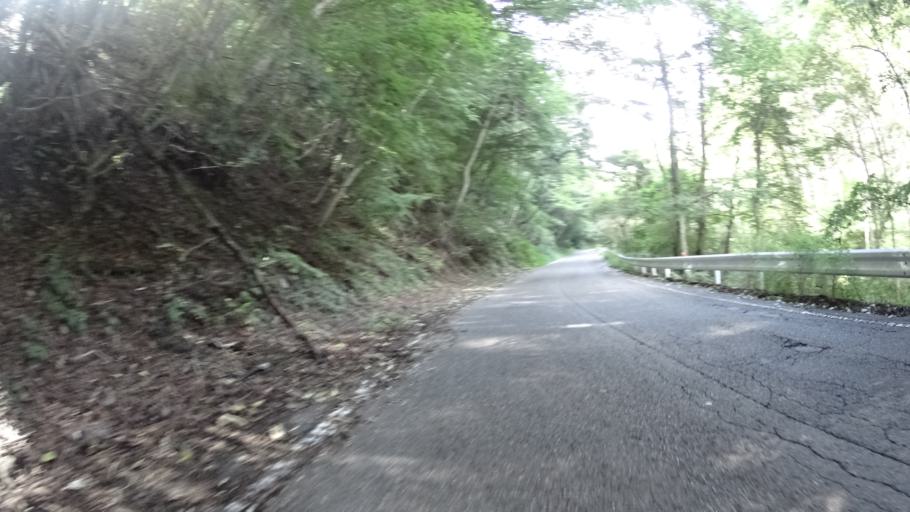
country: JP
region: Yamanashi
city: Nirasaki
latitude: 35.9075
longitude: 138.5402
